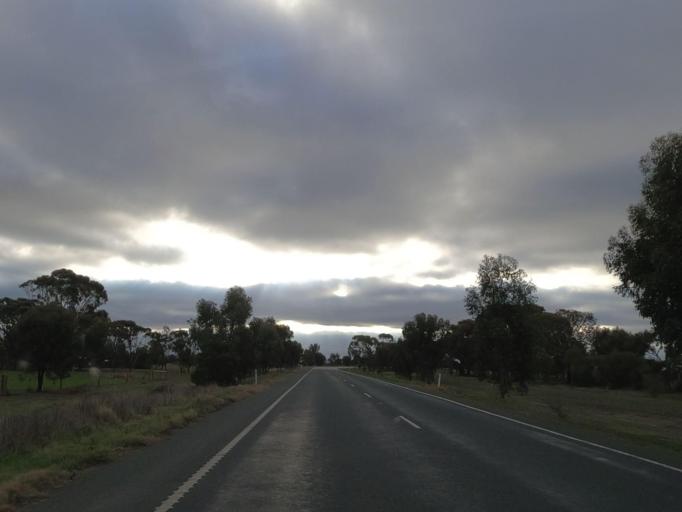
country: AU
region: Victoria
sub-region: Swan Hill
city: Swan Hill
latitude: -35.7308
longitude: 143.8946
